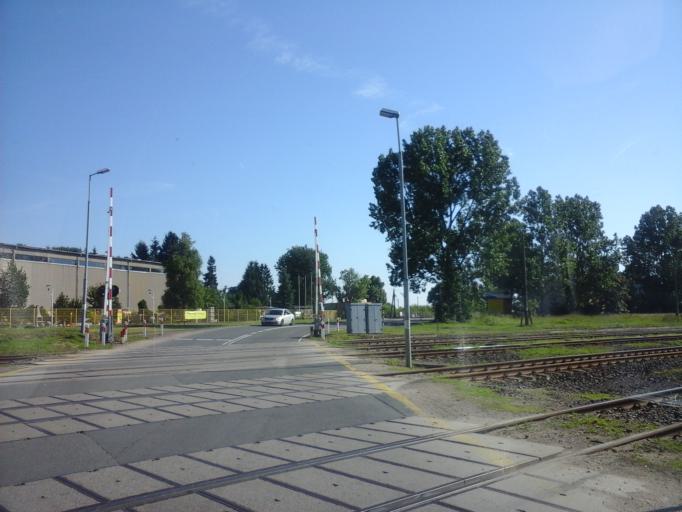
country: PL
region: West Pomeranian Voivodeship
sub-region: Powiat drawski
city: Drawsko Pomorskie
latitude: 53.5167
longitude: 15.7756
